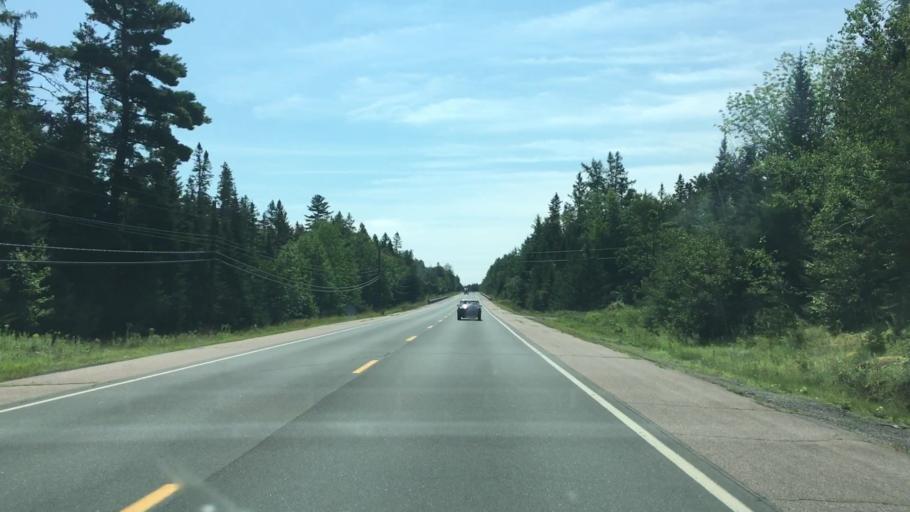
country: US
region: Maine
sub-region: Washington County
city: Calais
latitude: 45.1494
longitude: -67.1710
